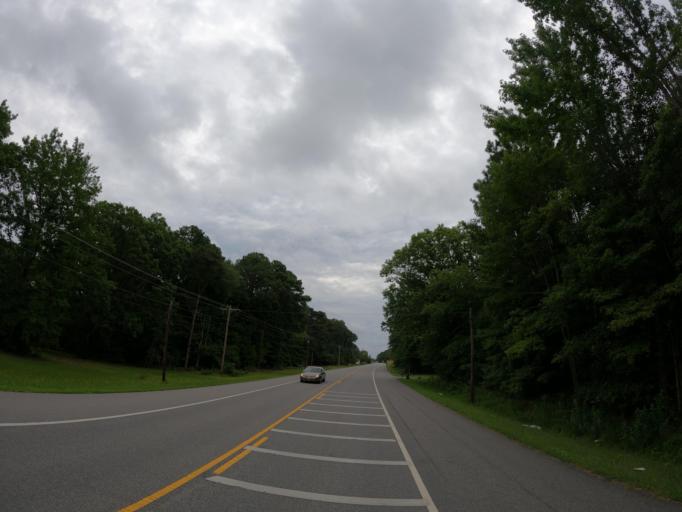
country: US
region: Maryland
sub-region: Saint Mary's County
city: Lexington Park
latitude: 38.1504
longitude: -76.5137
